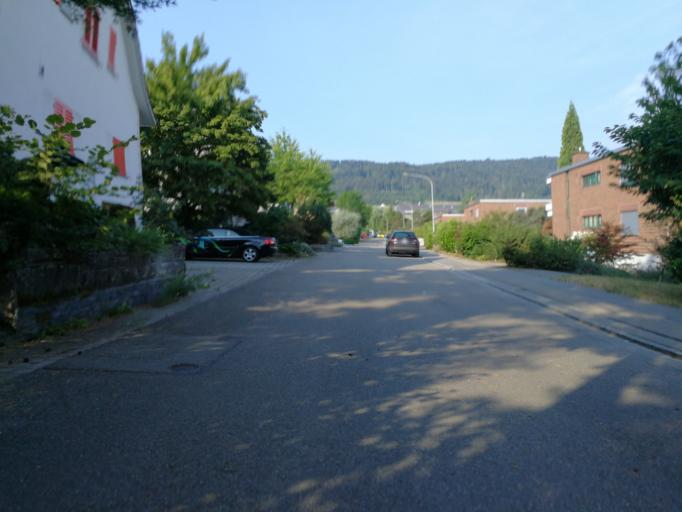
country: CH
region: Zurich
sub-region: Bezirk Uster
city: Egg
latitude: 47.3028
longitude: 8.6940
